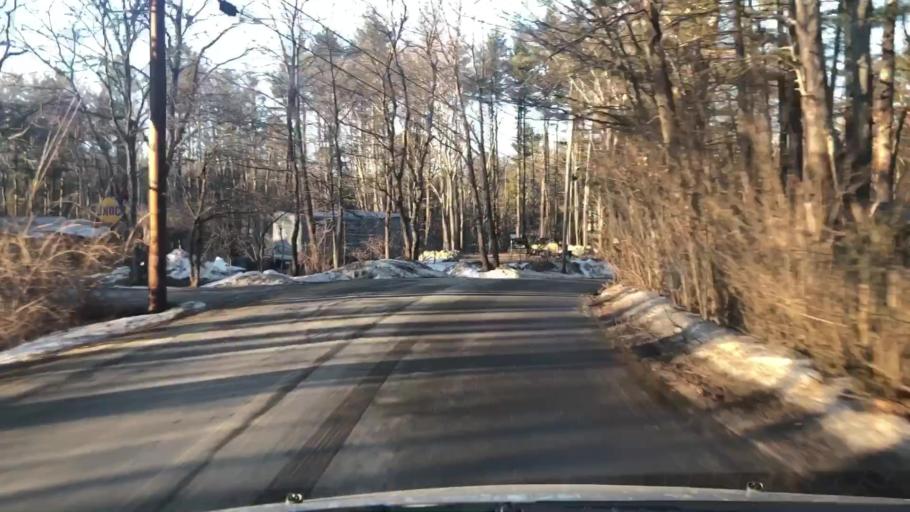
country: US
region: New Hampshire
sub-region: Hillsborough County
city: Milford
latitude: 42.8050
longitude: -71.6472
